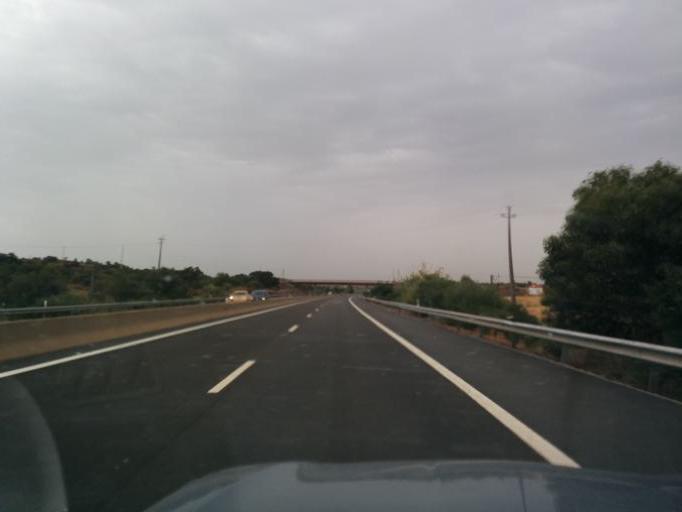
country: PT
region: Faro
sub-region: Vila Real de Santo Antonio
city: Monte Gordo
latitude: 37.1987
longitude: -7.5224
